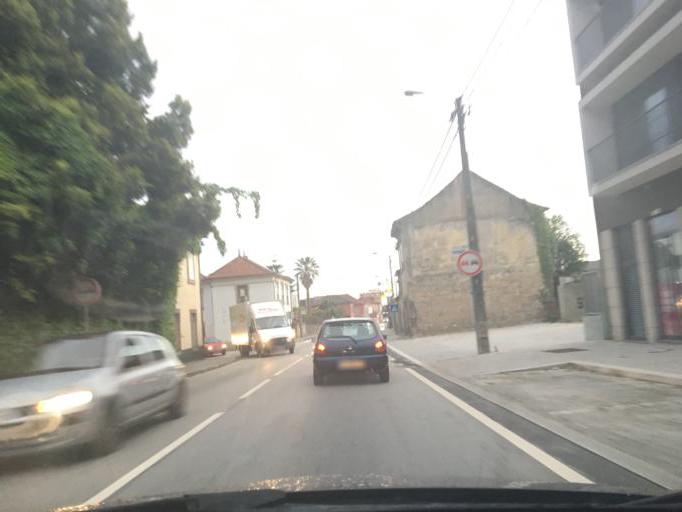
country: PT
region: Porto
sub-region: Maia
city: Anta
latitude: 41.2731
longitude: -8.6091
